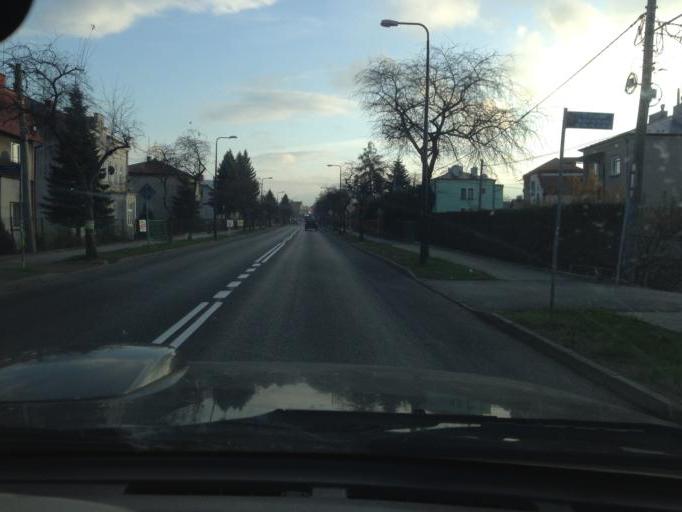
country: PL
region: Subcarpathian Voivodeship
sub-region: Powiat jasielski
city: Jaslo
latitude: 49.7561
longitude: 21.4725
